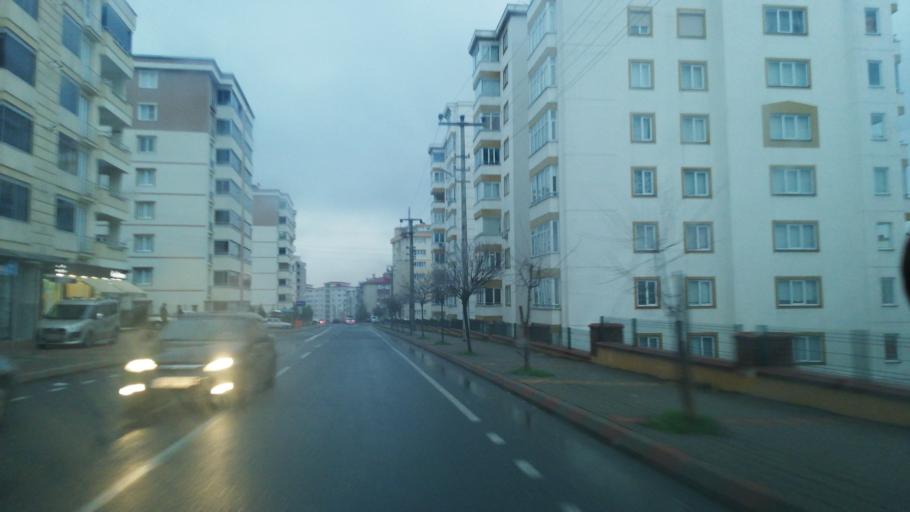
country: TR
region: Kahramanmaras
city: Kahramanmaras
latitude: 37.5999
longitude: 36.8851
